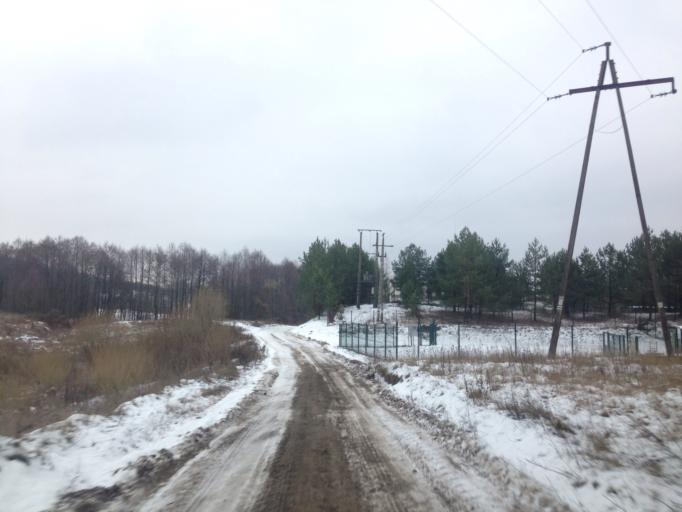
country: PL
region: Kujawsko-Pomorskie
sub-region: Powiat brodnicki
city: Gorzno
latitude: 53.2063
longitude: 19.6441
